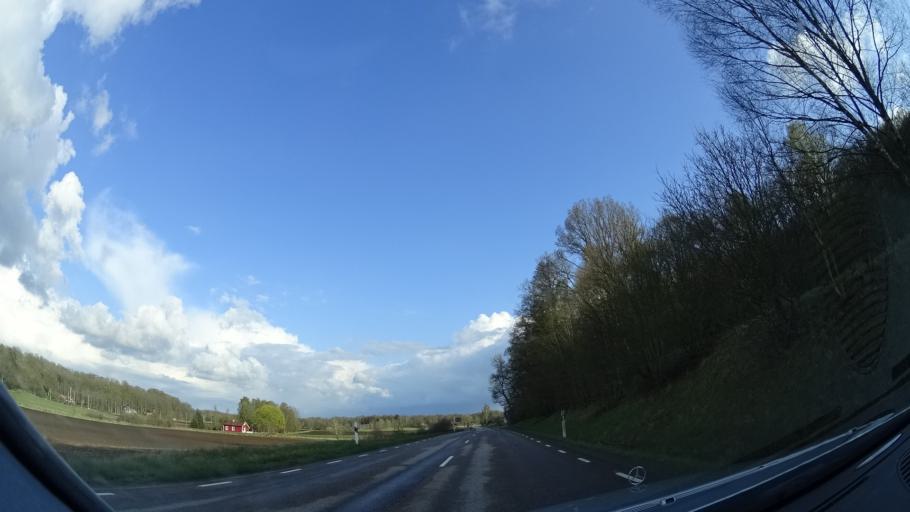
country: SE
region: Skane
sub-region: Klippans Kommun
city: Ljungbyhed
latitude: 56.0284
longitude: 13.2651
